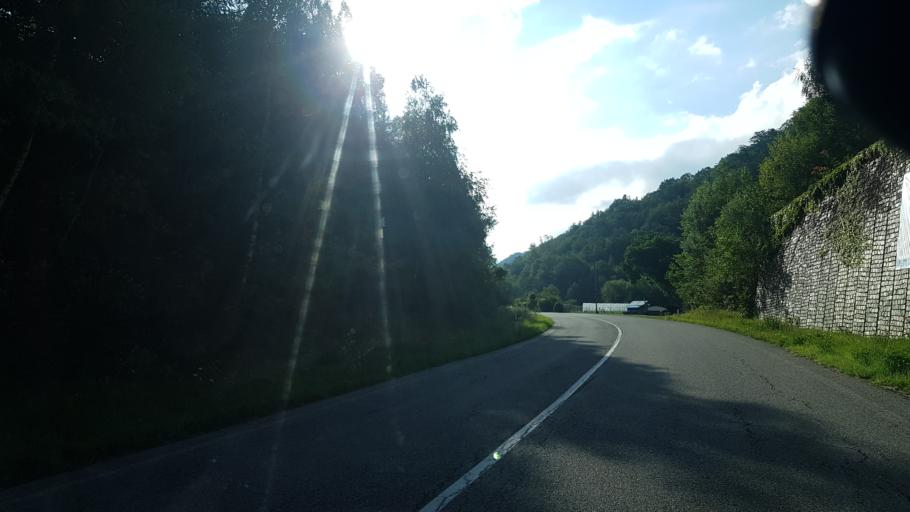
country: IT
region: Piedmont
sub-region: Provincia di Cuneo
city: Sampeyre
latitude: 44.5768
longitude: 7.2181
